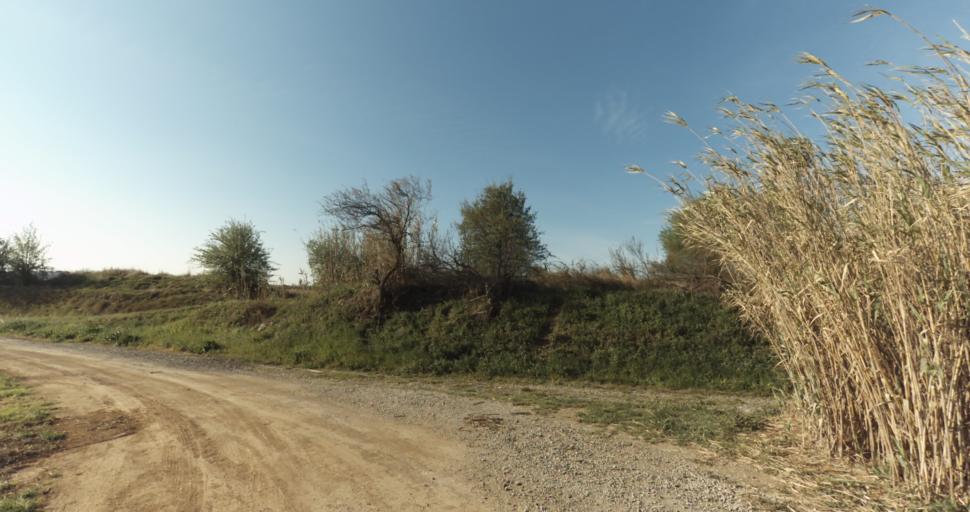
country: FR
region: Languedoc-Roussillon
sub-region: Departement de l'Herault
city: Marseillan
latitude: 43.3704
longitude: 3.5122
